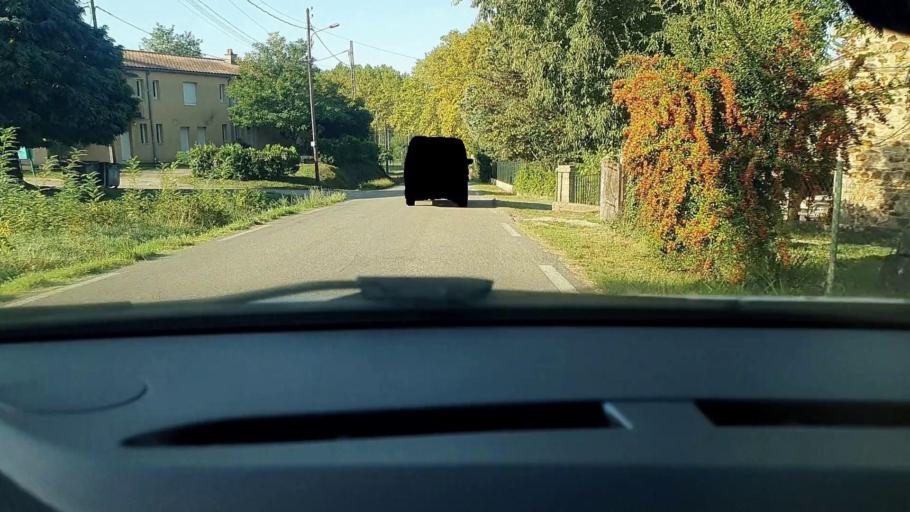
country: FR
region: Languedoc-Roussillon
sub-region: Departement du Gard
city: Besseges
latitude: 44.3169
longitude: 4.1324
